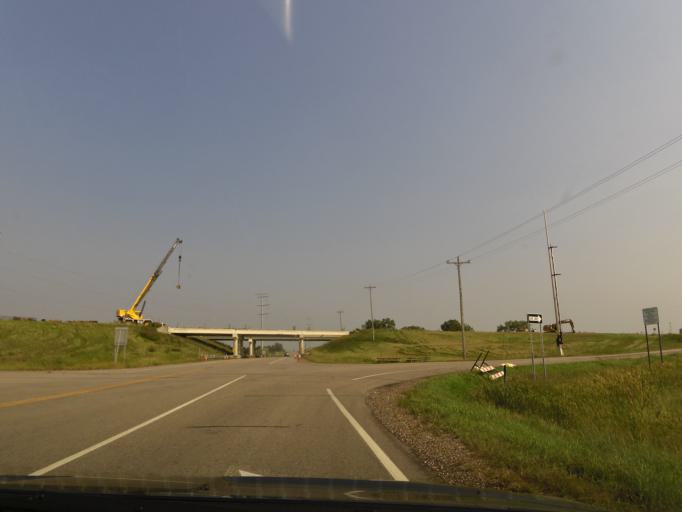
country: US
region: Minnesota
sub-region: Grant County
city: Elbow Lake
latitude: 45.9987
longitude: -95.7315
